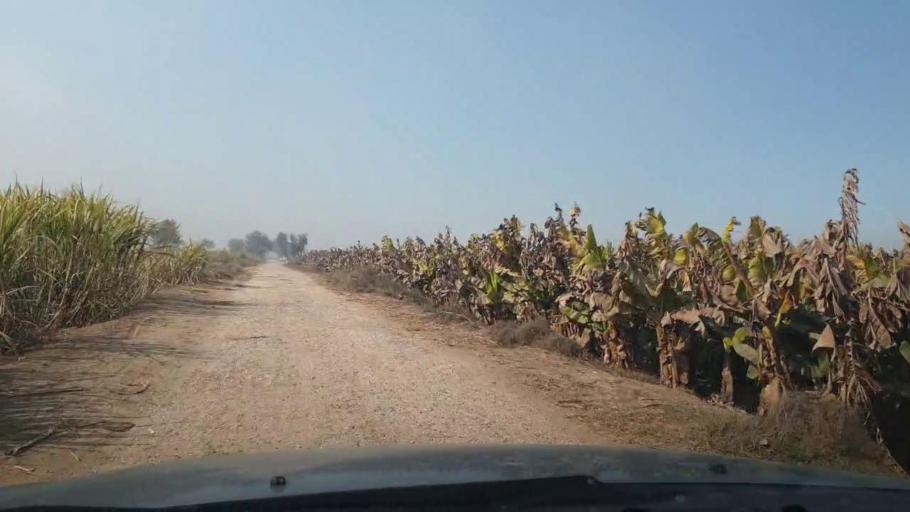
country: PK
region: Sindh
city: Ghotki
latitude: 28.0272
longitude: 69.2552
